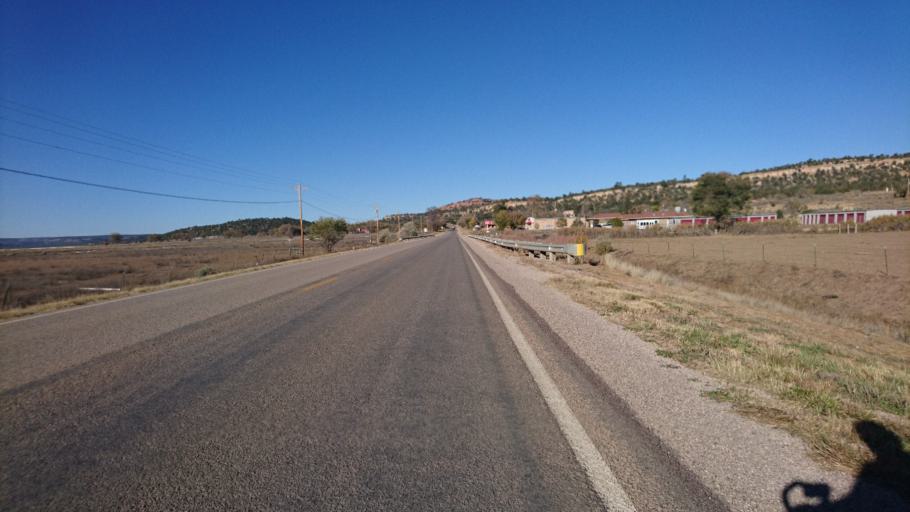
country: US
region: New Mexico
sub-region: McKinley County
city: Black Rock
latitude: 35.1333
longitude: -108.5059
